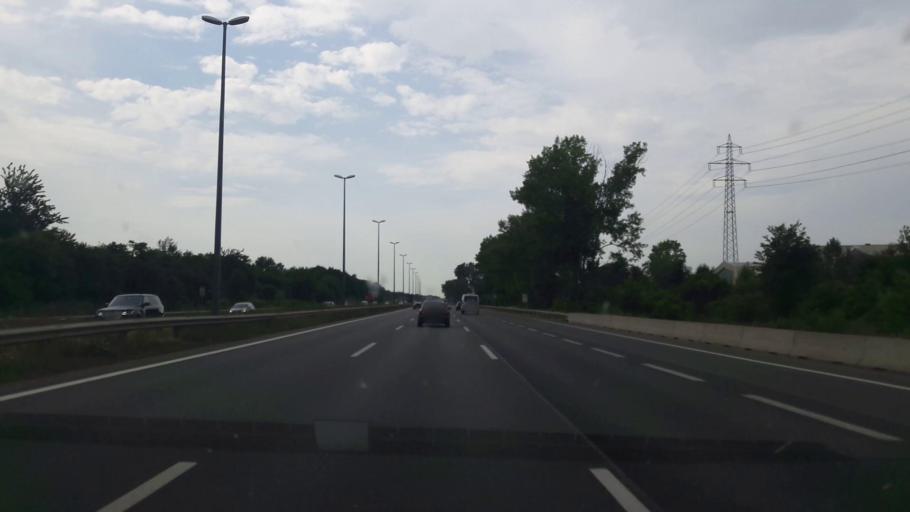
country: AT
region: Lower Austria
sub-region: Politischer Bezirk Korneuburg
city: Langenzersdorf
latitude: 48.2823
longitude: 16.3645
